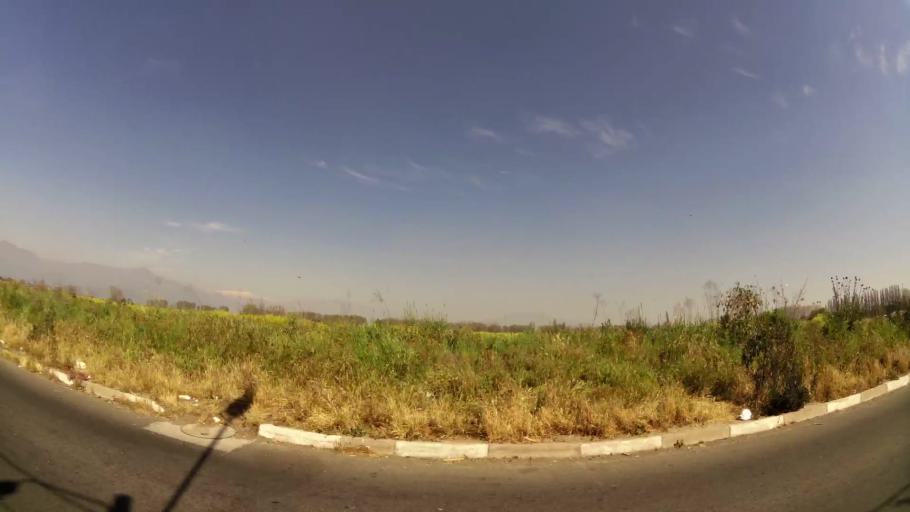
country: CL
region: Santiago Metropolitan
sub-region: Provincia de Santiago
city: La Pintana
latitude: -33.5657
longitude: -70.6255
